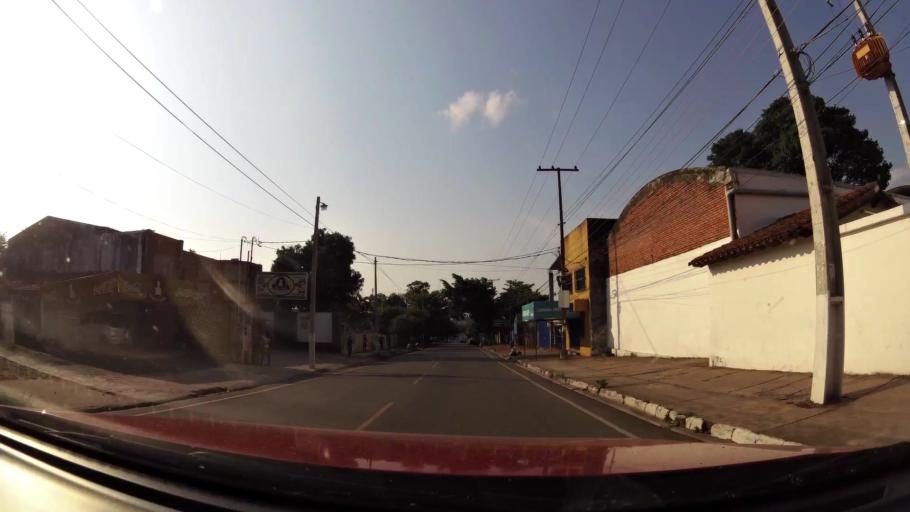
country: PY
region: Central
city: Lambare
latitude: -25.3438
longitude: -57.5893
